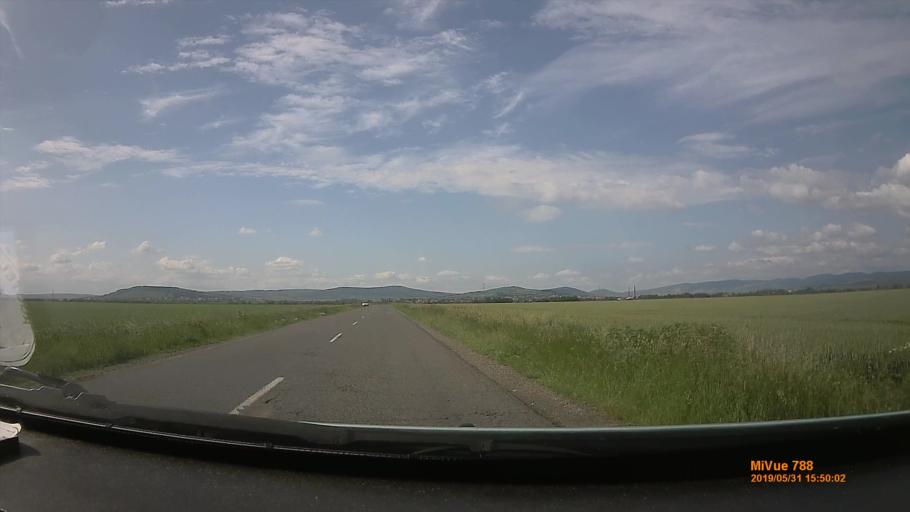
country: HU
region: Borsod-Abauj-Zemplen
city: Taktaszada
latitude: 48.1301
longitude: 21.2057
